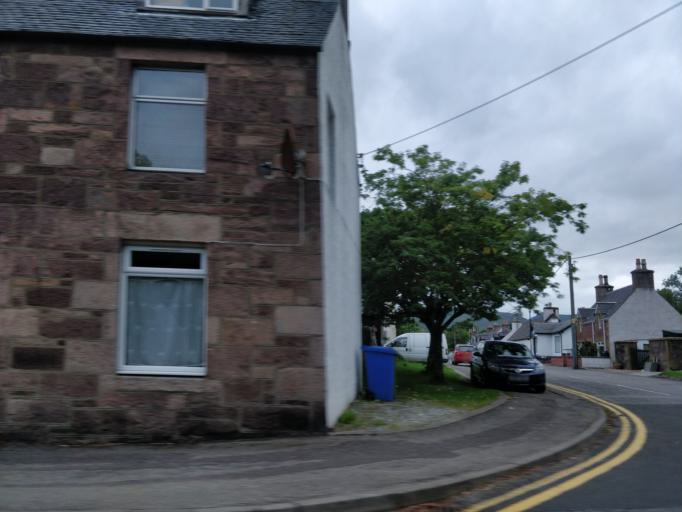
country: GB
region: Scotland
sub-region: Highland
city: Ullapool
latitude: 57.8975
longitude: -5.1555
